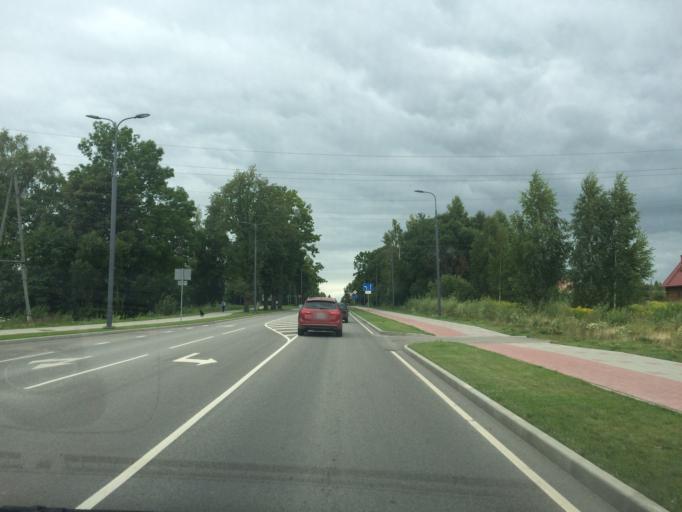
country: LV
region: Rezekne
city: Rezekne
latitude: 56.5326
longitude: 27.3468
